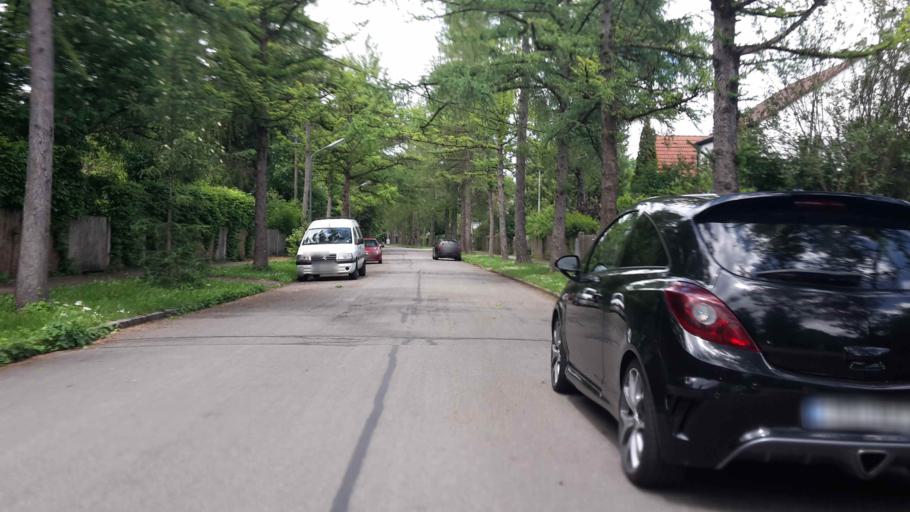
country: DE
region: Bavaria
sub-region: Upper Bavaria
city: Pasing
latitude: 48.1734
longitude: 11.4838
